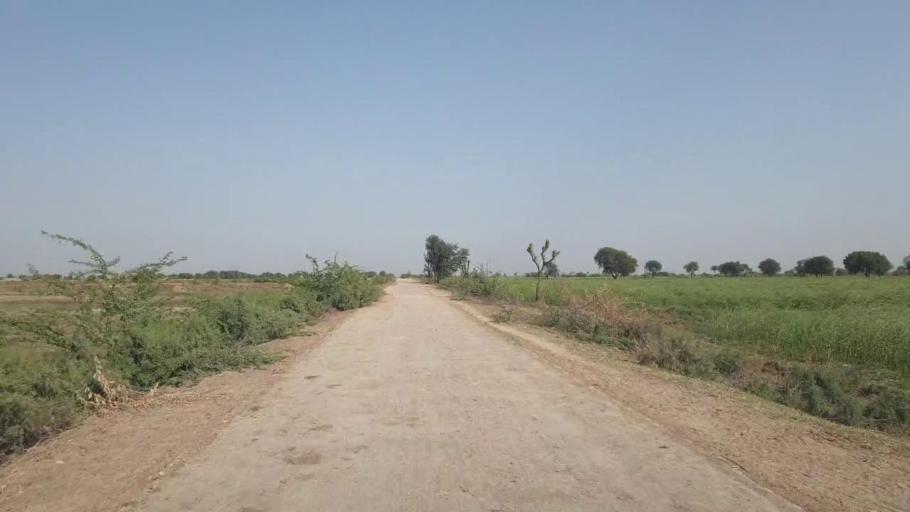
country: PK
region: Sindh
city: Dhoro Naro
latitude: 25.4419
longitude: 69.5426
